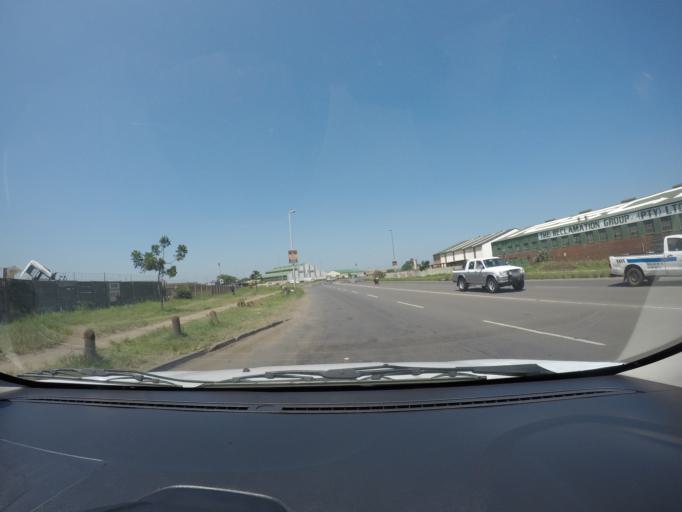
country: ZA
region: KwaZulu-Natal
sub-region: uThungulu District Municipality
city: Richards Bay
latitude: -28.7521
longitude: 32.0287
